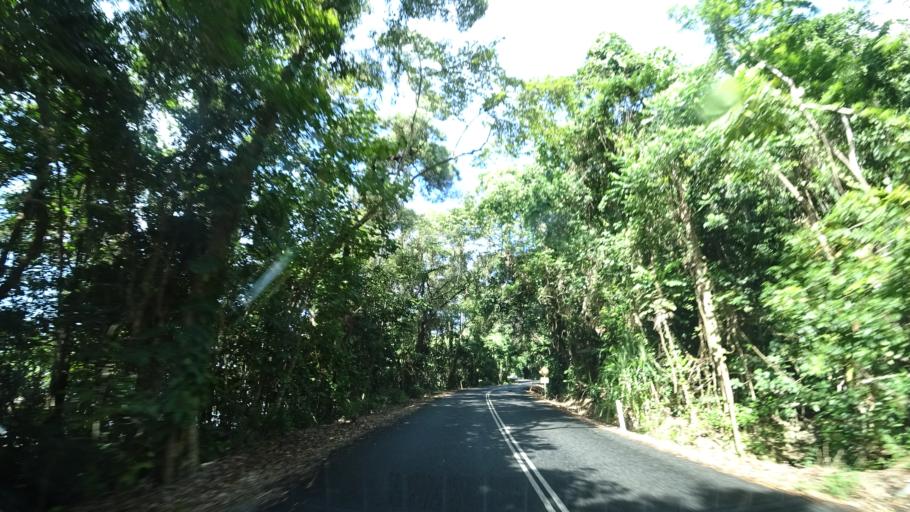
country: AU
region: Queensland
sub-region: Cairns
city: Port Douglas
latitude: -16.1157
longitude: 145.4571
